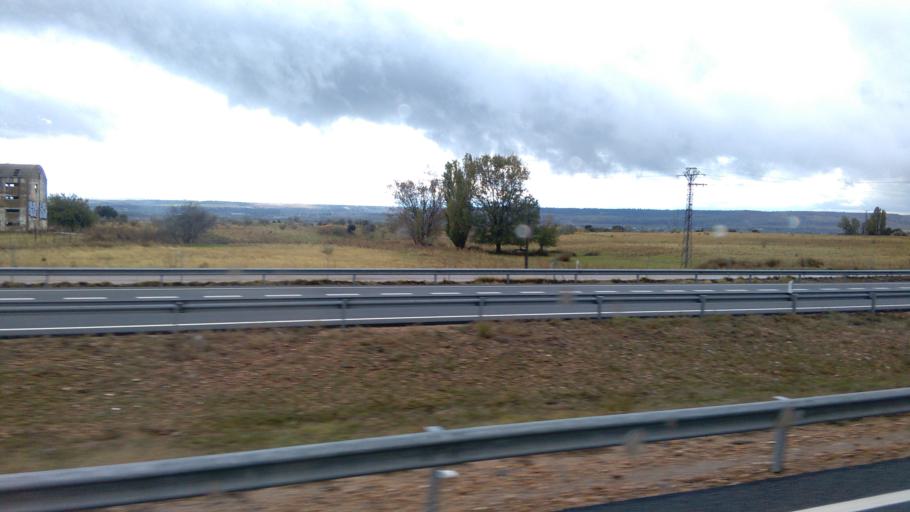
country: ES
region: Castille-La Mancha
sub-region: Province of Toledo
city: Cazalegas
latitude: 39.9911
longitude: -4.6987
